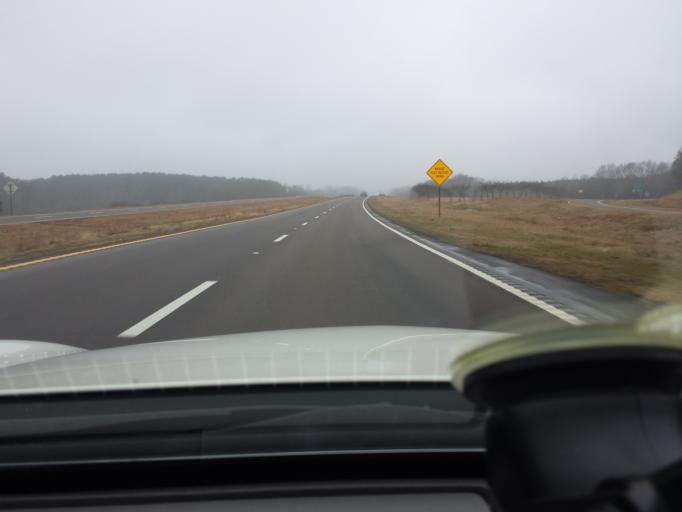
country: US
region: Mississippi
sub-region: Leake County
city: Carthage
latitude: 32.7710
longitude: -89.5372
